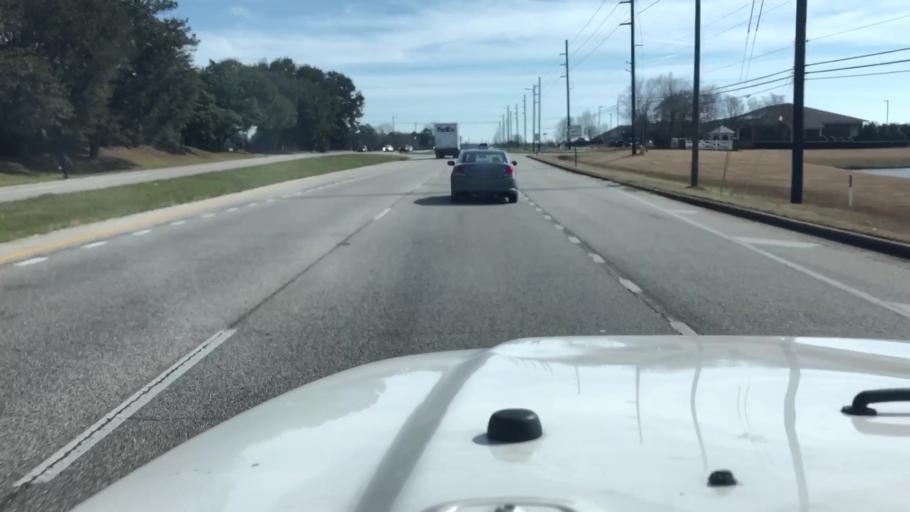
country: US
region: Alabama
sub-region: Montgomery County
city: Pike Road
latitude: 32.3799
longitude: -86.1583
